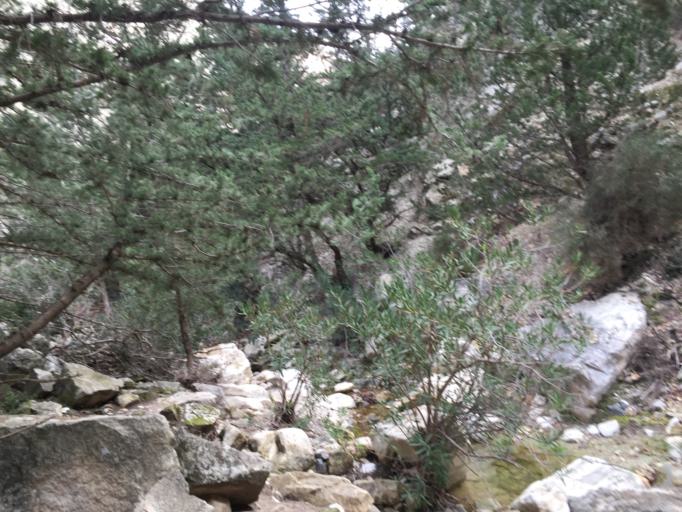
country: CY
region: Pafos
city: Pegeia
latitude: 34.9268
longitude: 32.3550
